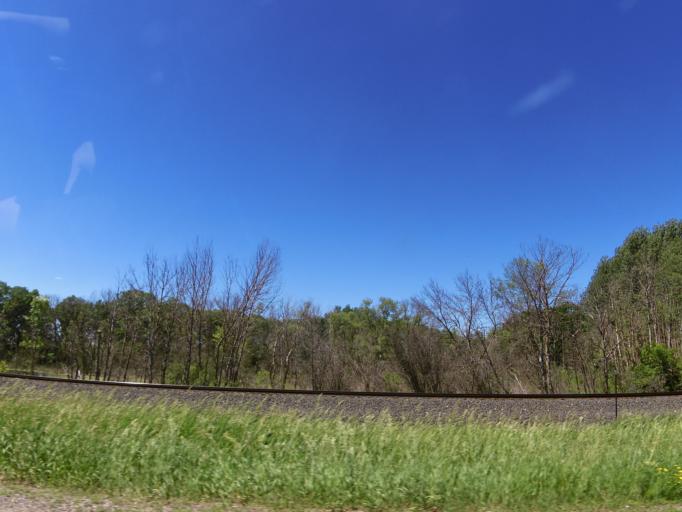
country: US
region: Minnesota
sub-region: Becker County
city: Detroit Lakes
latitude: 46.8799
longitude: -95.8985
